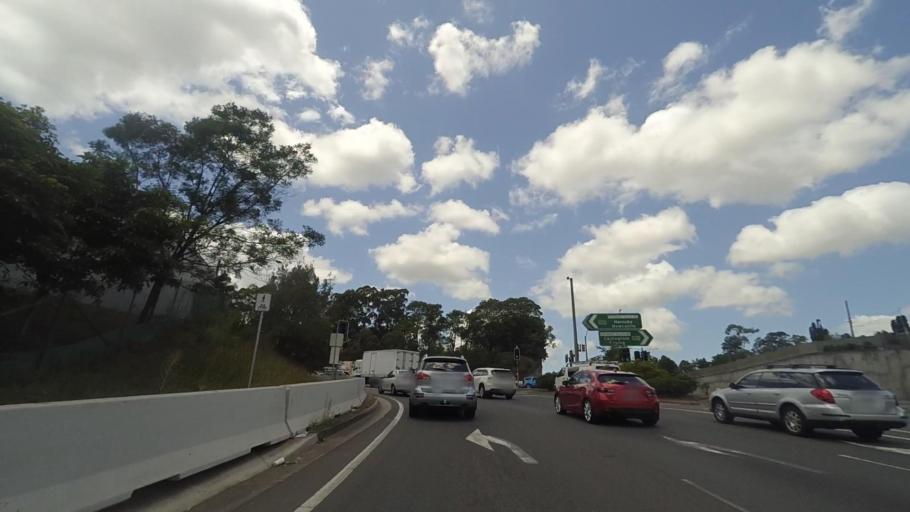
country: AU
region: New South Wales
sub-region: The Hills Shire
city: West Pennant
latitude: -33.7585
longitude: 151.0483
